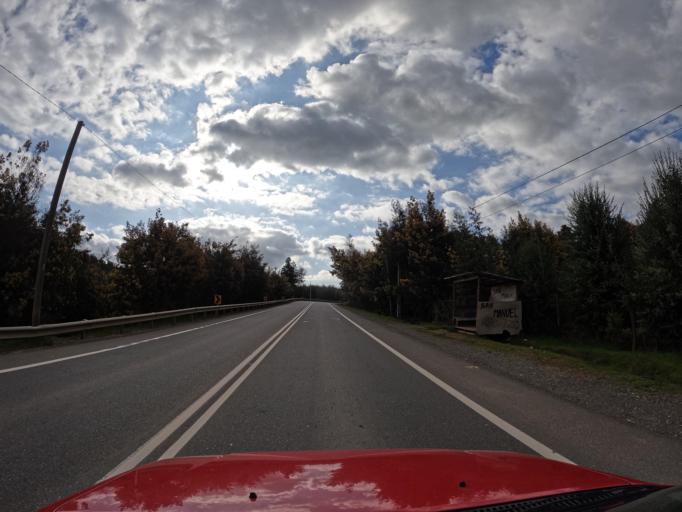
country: CL
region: Maule
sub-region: Provincia de Talca
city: Constitucion
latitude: -35.5543
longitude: -72.1421
